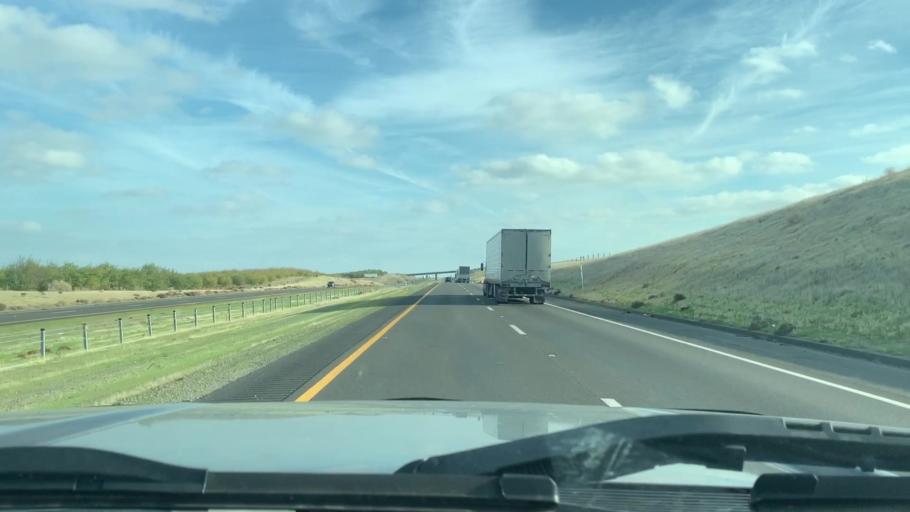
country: US
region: California
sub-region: Kings County
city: Avenal
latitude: 36.0584
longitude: -120.0718
